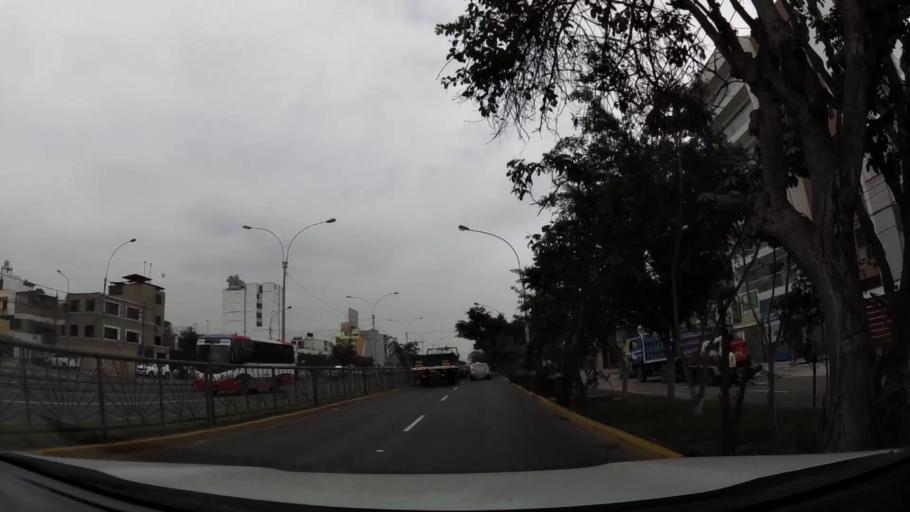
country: PE
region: Lima
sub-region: Lima
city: Surco
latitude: -12.1210
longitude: -77.0066
